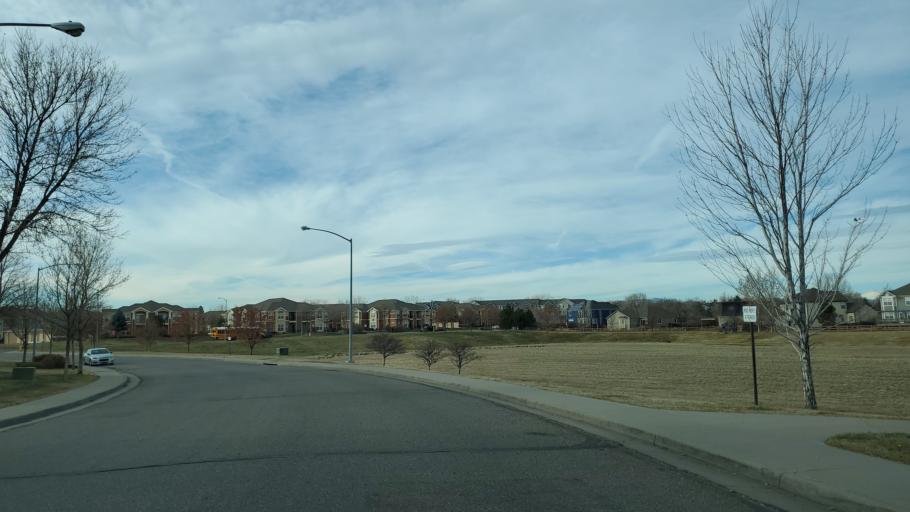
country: US
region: Colorado
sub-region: Adams County
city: Northglenn
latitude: 39.9169
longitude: -104.9459
